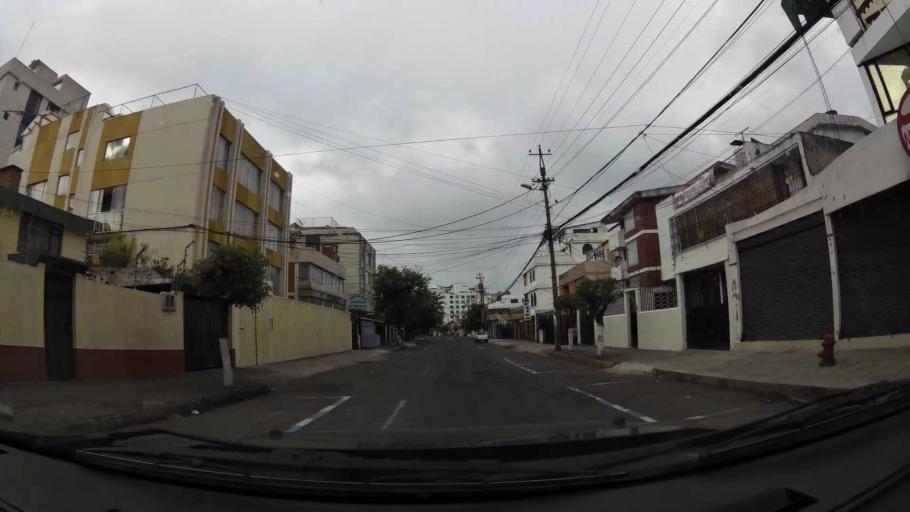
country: EC
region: Pichincha
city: Quito
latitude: -0.1906
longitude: -78.4911
